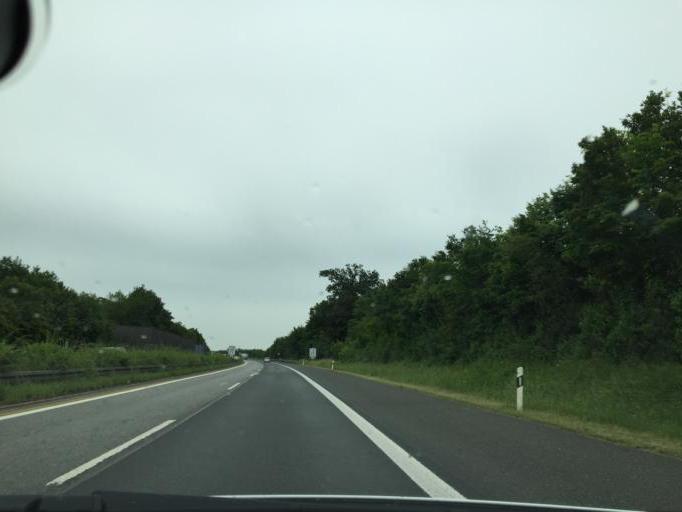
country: DE
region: Bavaria
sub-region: Regierungsbezirk Unterfranken
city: Gadheim
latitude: 50.0110
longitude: 10.3488
